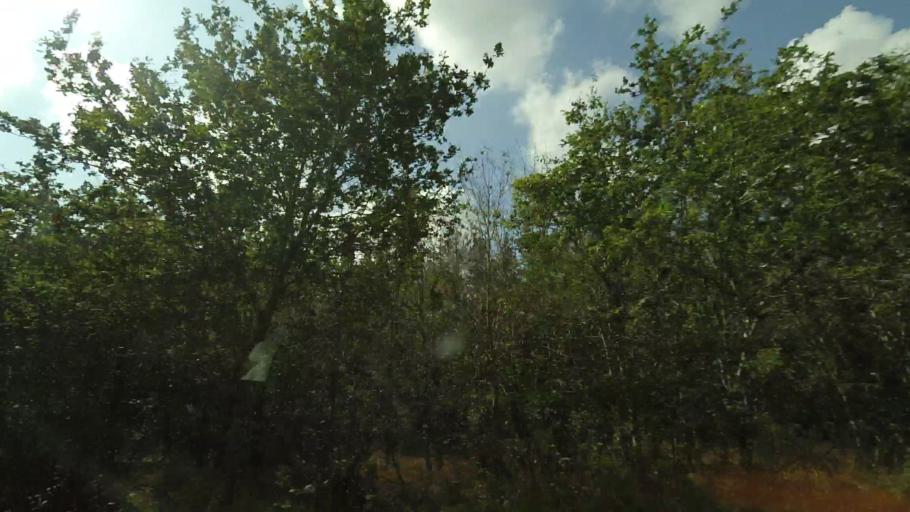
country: DK
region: Central Jutland
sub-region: Norddjurs Kommune
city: Auning
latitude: 56.5121
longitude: 10.4079
